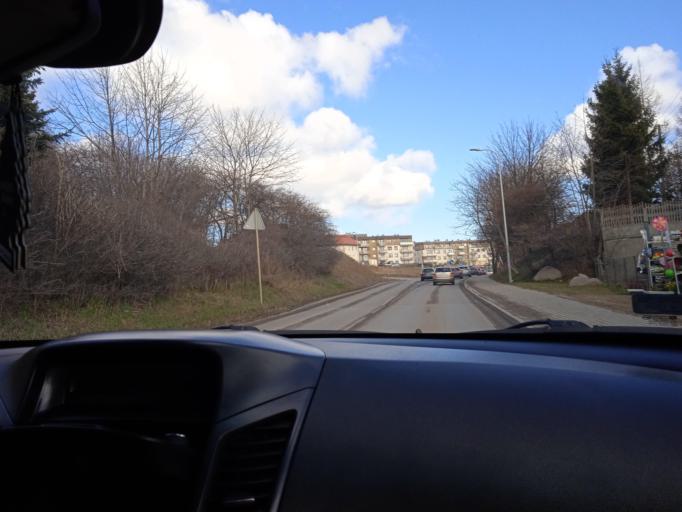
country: PL
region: Pomeranian Voivodeship
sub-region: Powiat gdanski
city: Kowale
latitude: 54.3295
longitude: 18.5542
